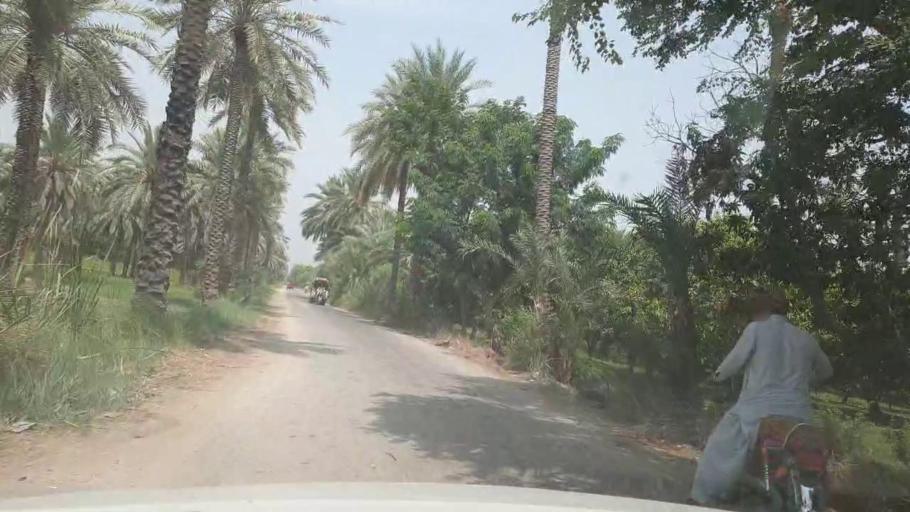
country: PK
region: Sindh
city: Kot Diji
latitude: 27.3617
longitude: 68.7018
